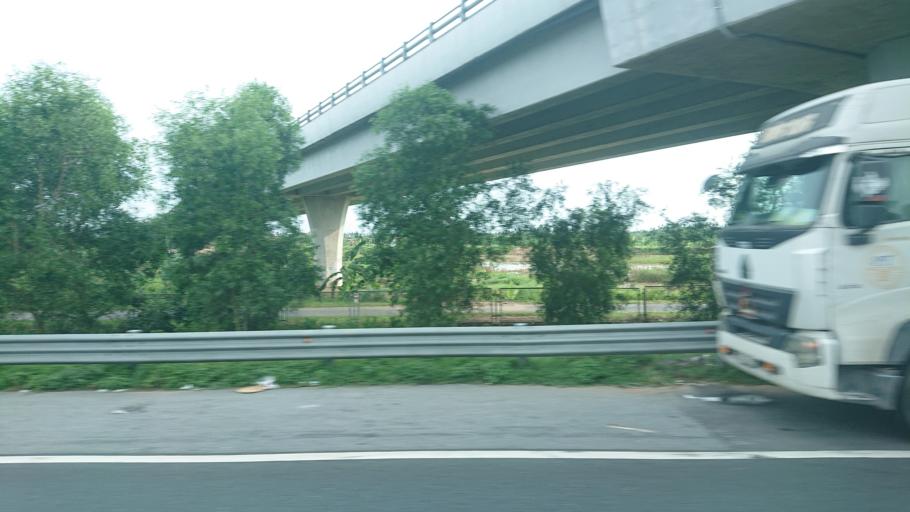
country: VN
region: Hai Phong
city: An Lao
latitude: 20.8179
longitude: 106.4852
